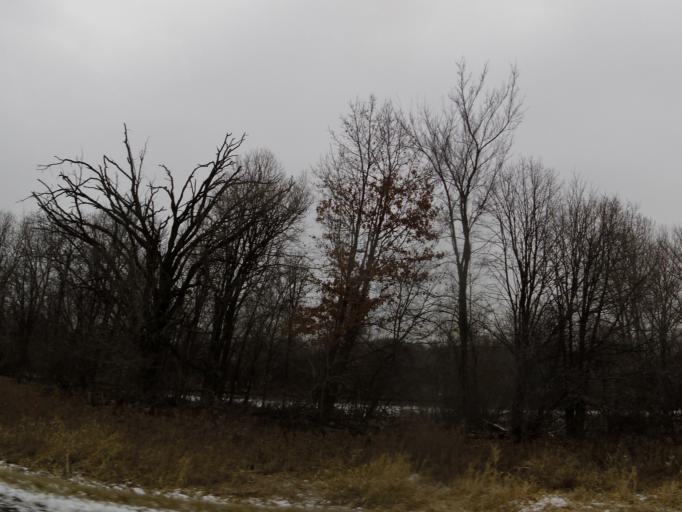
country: US
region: Minnesota
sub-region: Hennepin County
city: Independence
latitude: 45.0358
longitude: -93.7444
